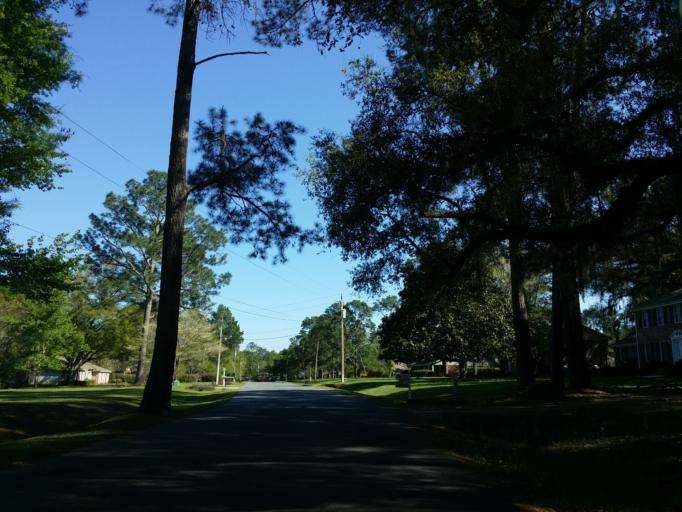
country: US
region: Florida
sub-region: Leon County
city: Tallahassee
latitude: 30.4788
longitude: -84.1882
